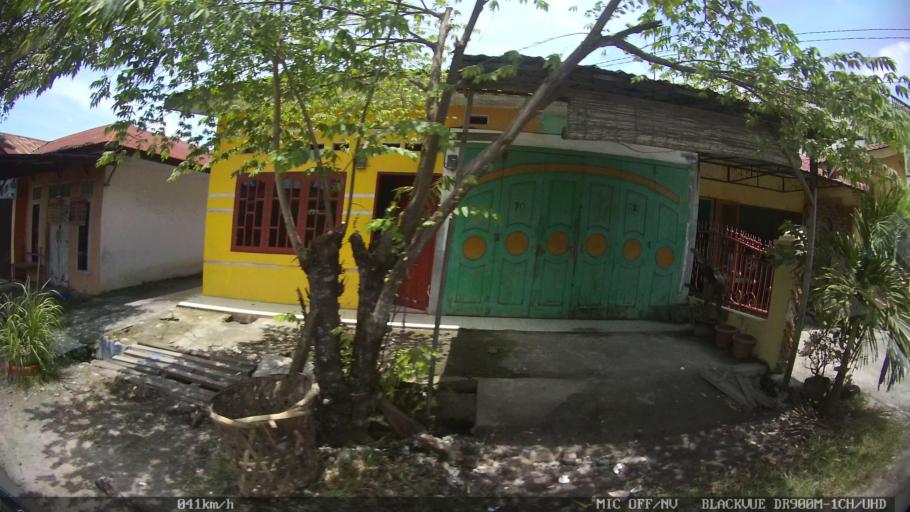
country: ID
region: North Sumatra
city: Percut
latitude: 3.5477
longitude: 98.8729
